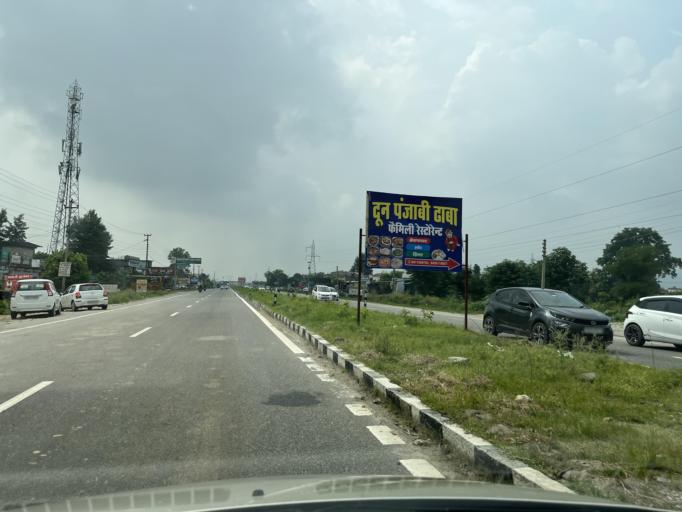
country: IN
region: Uttarakhand
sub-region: Dehradun
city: Raiwala
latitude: 30.0887
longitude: 78.1862
